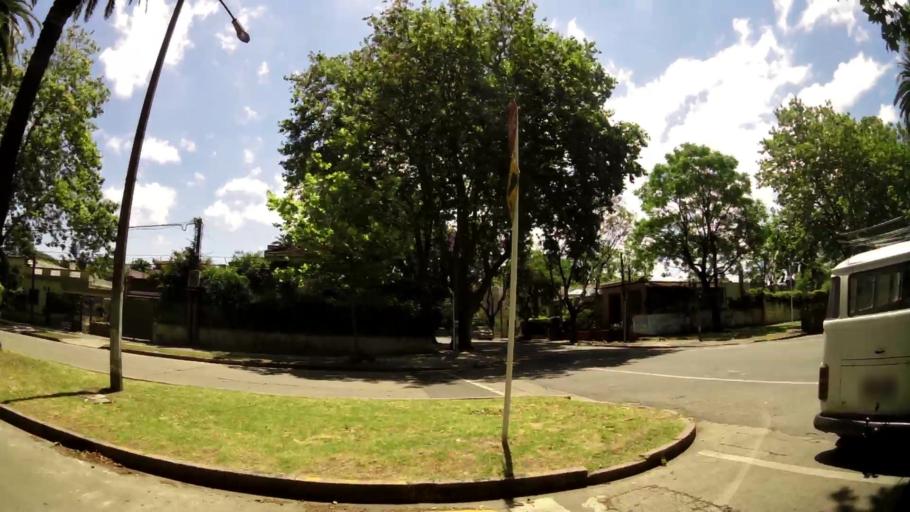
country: UY
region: Montevideo
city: Montevideo
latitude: -34.8657
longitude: -56.1980
